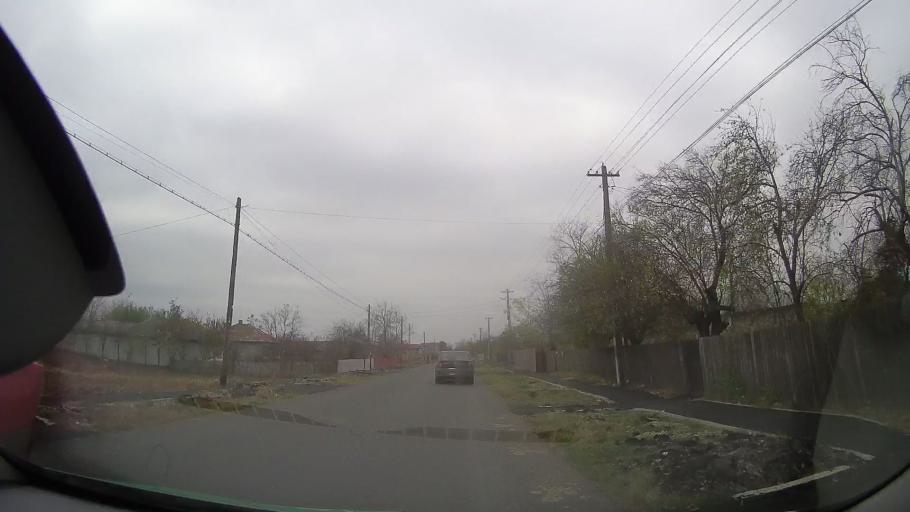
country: RO
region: Buzau
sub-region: Comuna Pogoanele
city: Pogoanele
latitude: 44.9216
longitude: 26.9933
